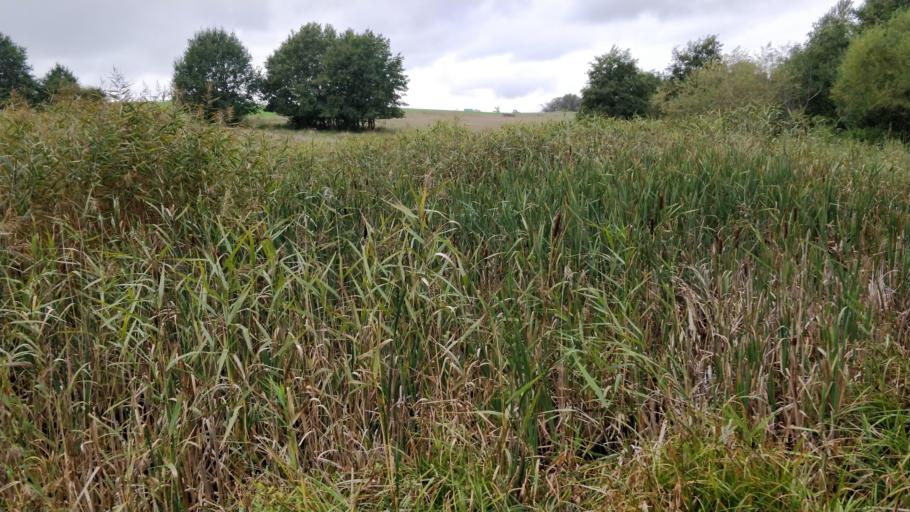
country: DK
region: Capital Region
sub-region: Ballerup Kommune
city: Malov
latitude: 55.7601
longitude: 12.3149
